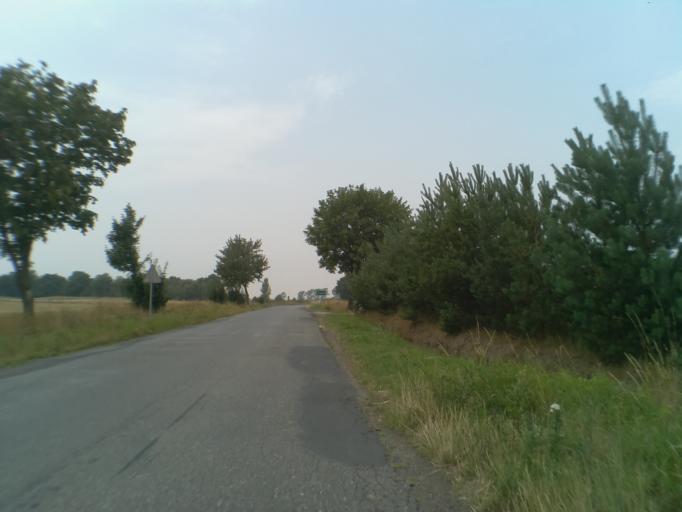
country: PL
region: Lower Silesian Voivodeship
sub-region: Powiat swidnicki
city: Swiebodzice
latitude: 50.8956
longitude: 16.3218
